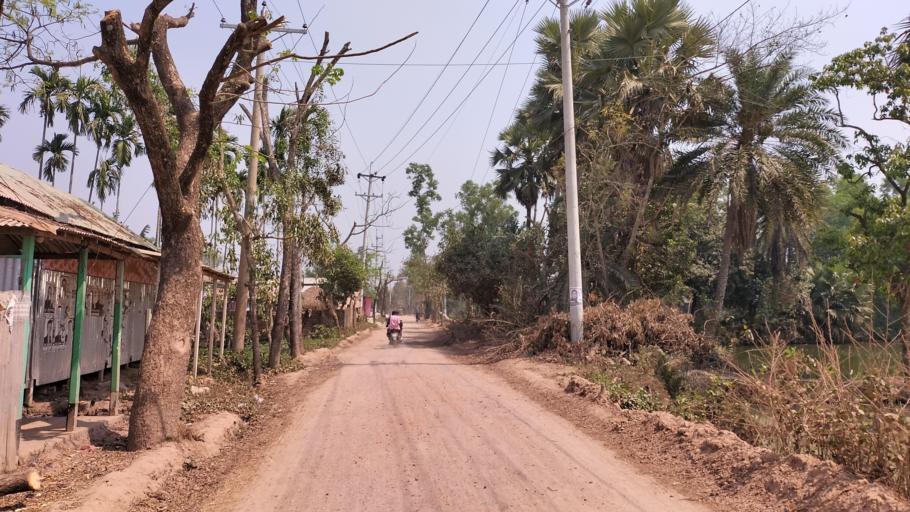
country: BD
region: Dhaka
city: Sakhipur
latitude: 24.3074
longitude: 90.3085
